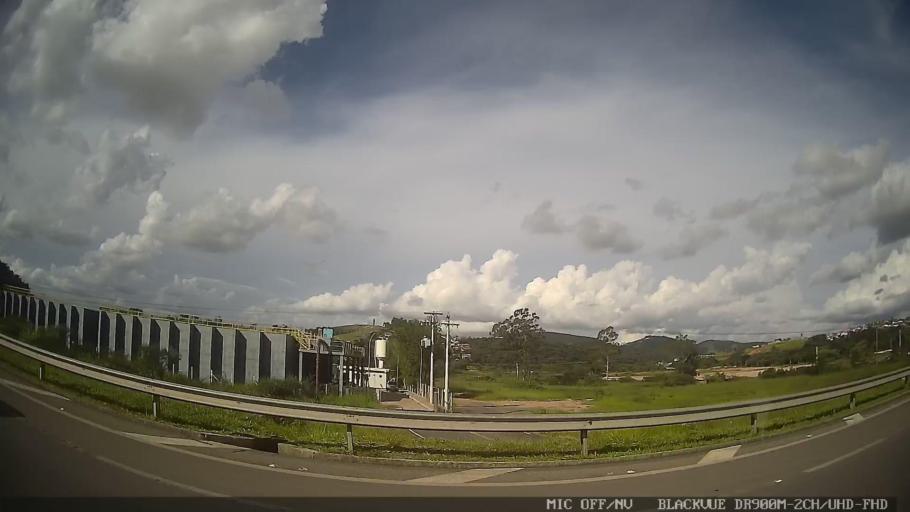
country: BR
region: Sao Paulo
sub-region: Bom Jesus Dos Perdoes
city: Bom Jesus dos Perdoes
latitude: -23.1282
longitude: -46.4650
